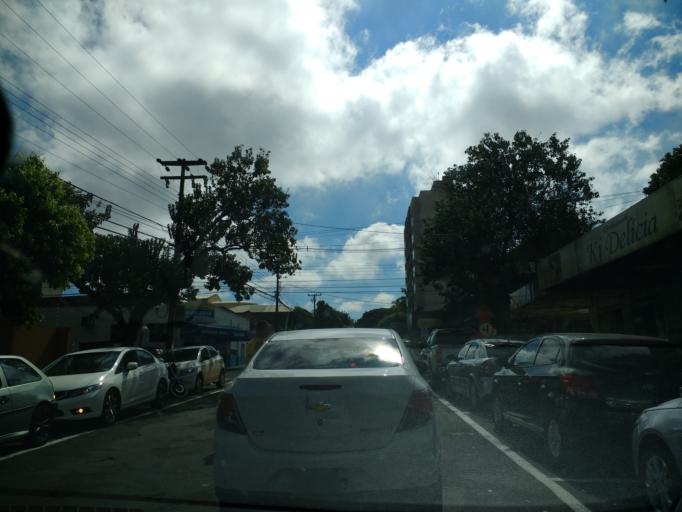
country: BR
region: Parana
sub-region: Umuarama
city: Umuarama
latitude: -23.7586
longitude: -53.2999
